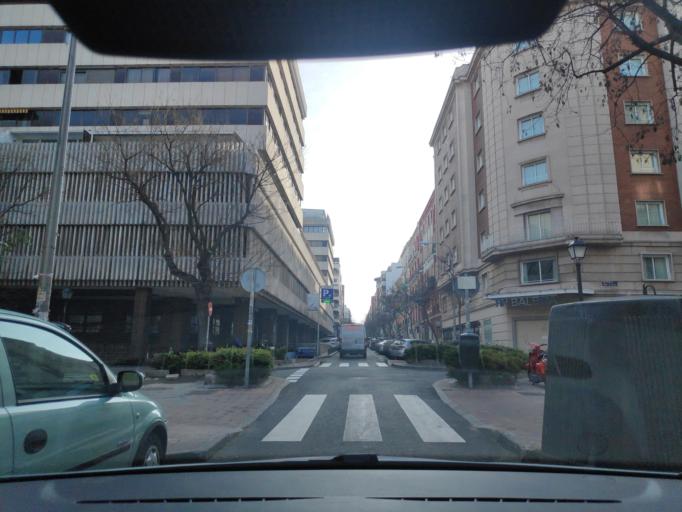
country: ES
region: Madrid
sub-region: Provincia de Madrid
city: Salamanca
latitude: 40.4361
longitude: -3.6821
